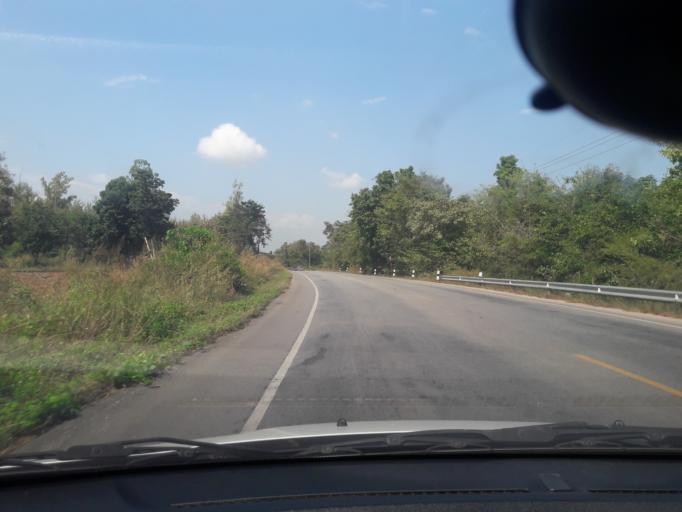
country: TH
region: Lampang
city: Mae Tha
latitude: 18.1908
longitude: 99.5253
